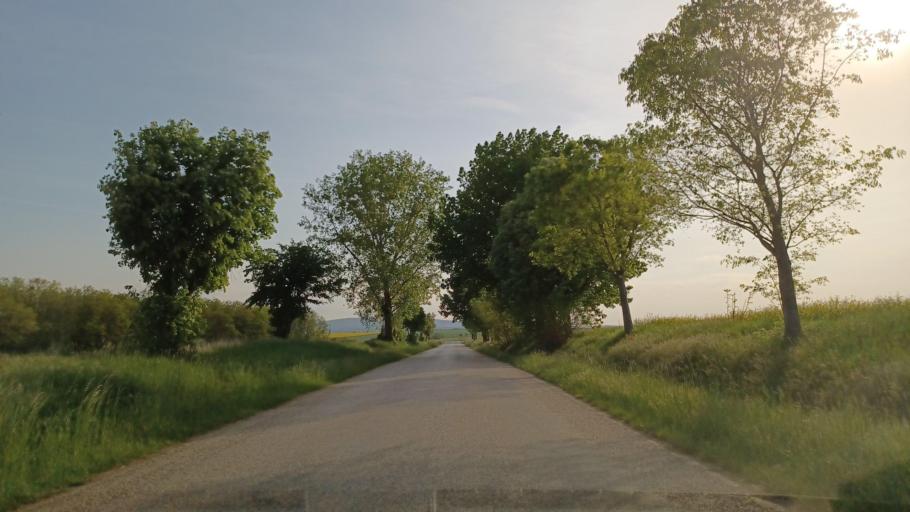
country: HU
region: Baranya
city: Kozarmisleny
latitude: 45.9471
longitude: 18.3646
